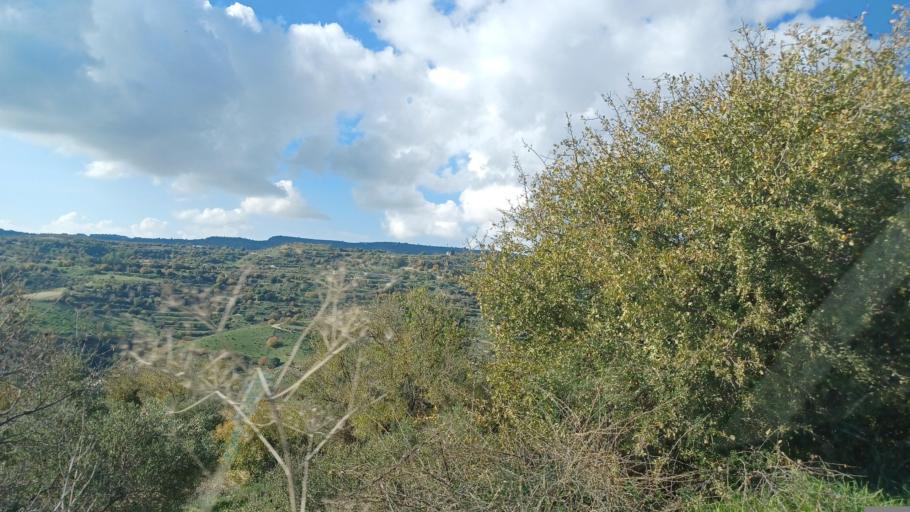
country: CY
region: Pafos
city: Mesogi
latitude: 34.8408
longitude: 32.5222
